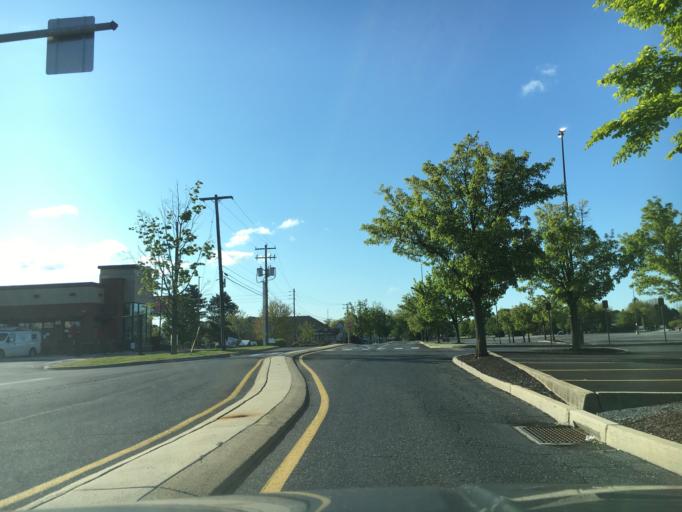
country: US
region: Pennsylvania
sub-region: Lehigh County
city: Hokendauqua
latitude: 40.6448
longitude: -75.4939
